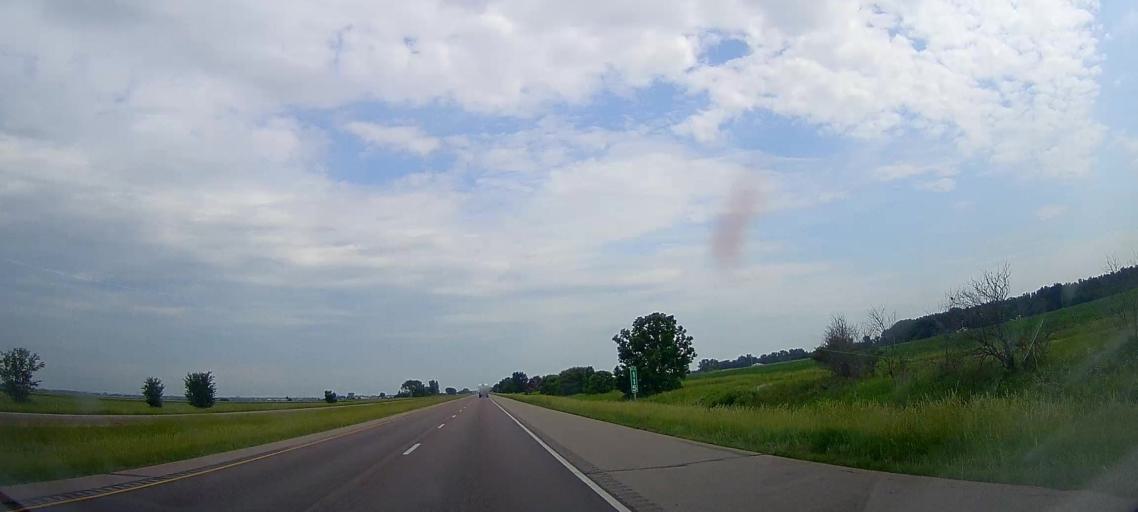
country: US
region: Iowa
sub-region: Monona County
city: Onawa
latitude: 42.0592
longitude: -96.1591
